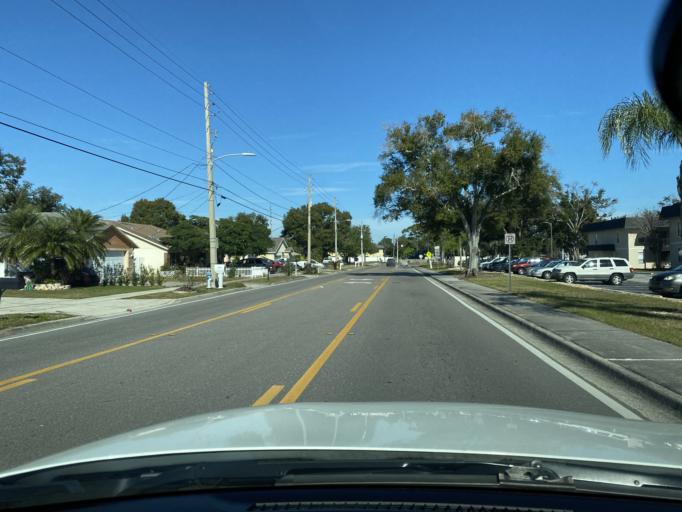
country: US
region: Florida
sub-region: Orange County
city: Azalea Park
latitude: 28.5228
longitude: -81.3145
